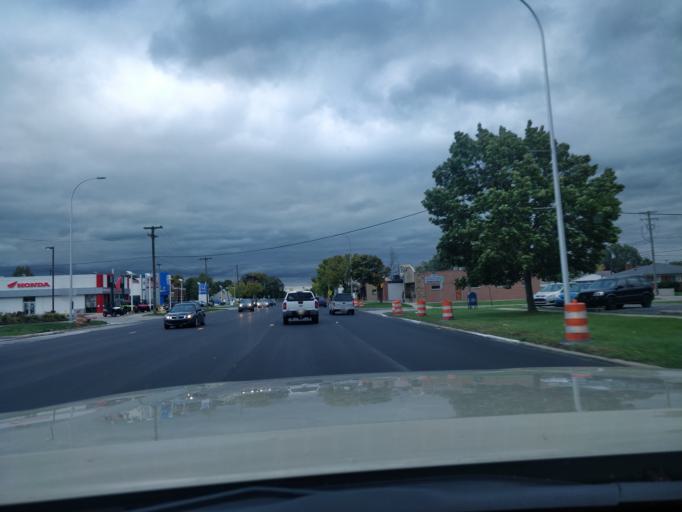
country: US
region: Michigan
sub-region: Wayne County
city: Southgate
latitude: 42.1990
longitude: -83.2087
